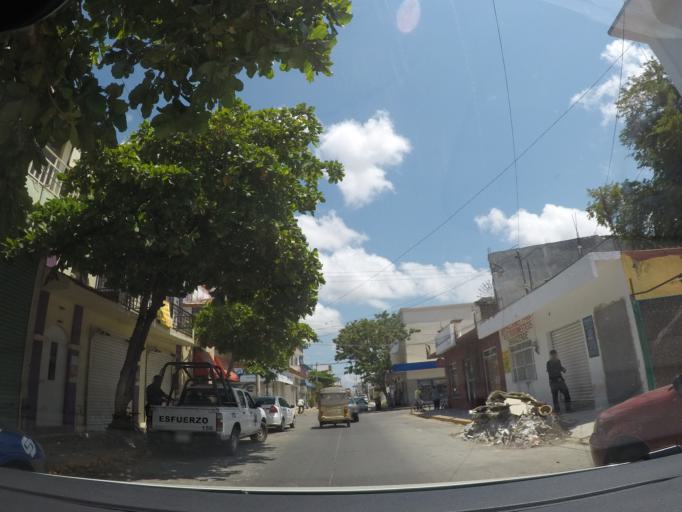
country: MX
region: Oaxaca
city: Juchitan de Zaragoza
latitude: 16.4388
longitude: -95.0222
